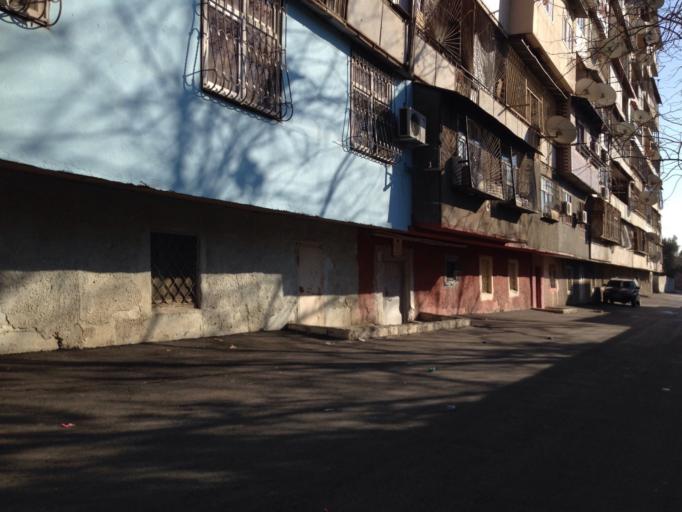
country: AZ
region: Baki
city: Baku
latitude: 40.3913
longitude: 49.8768
